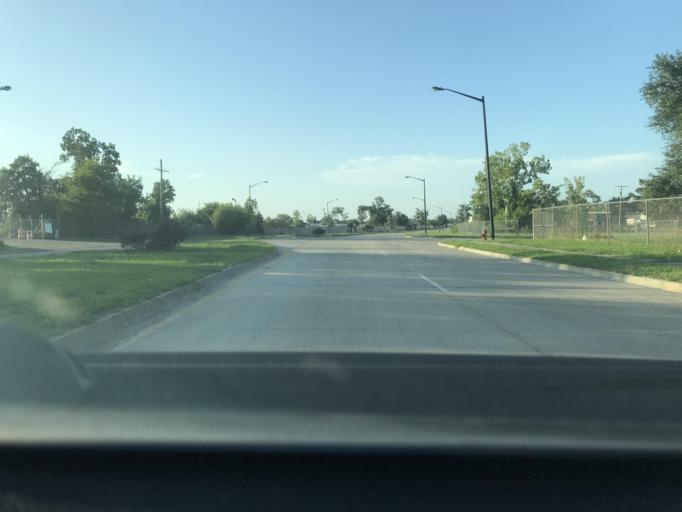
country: US
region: Louisiana
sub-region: Calcasieu Parish
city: Lake Charles
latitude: 30.2479
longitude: -93.2025
